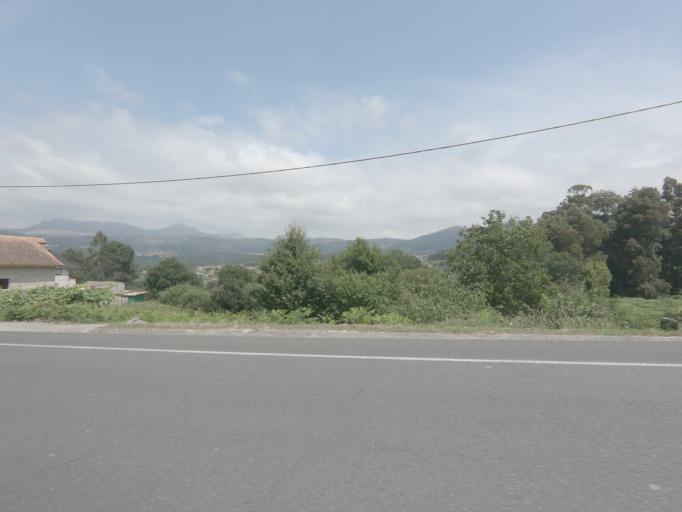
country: ES
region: Galicia
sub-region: Provincia de Pontevedra
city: Gondomar
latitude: 42.0991
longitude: -8.7595
